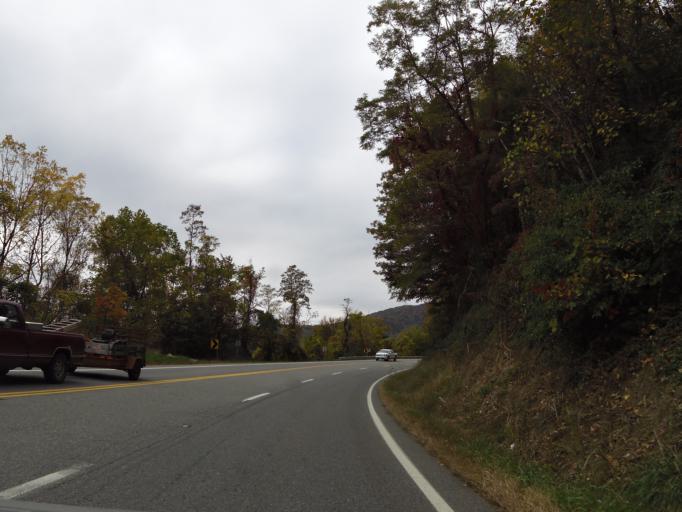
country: US
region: Virginia
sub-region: Carroll County
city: Cana
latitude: 36.6262
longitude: -80.6920
